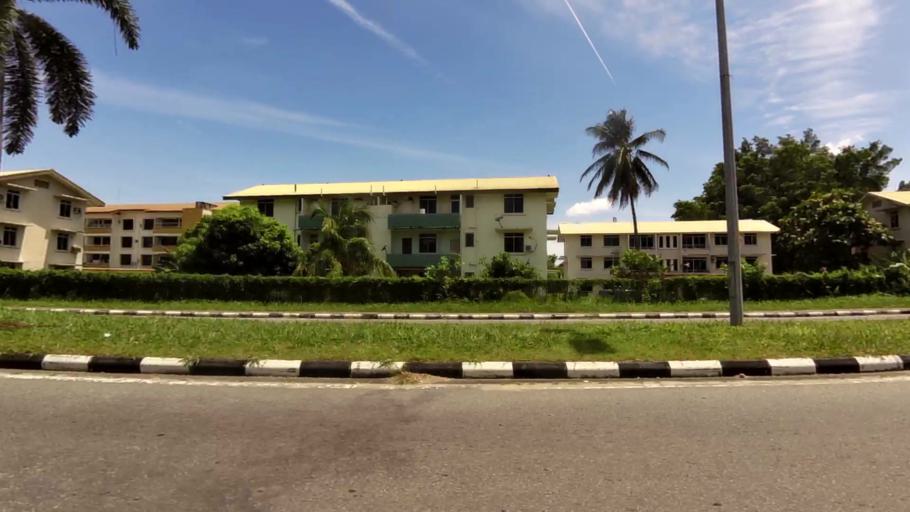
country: BN
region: Brunei and Muara
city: Bandar Seri Begawan
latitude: 4.9447
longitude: 114.9474
